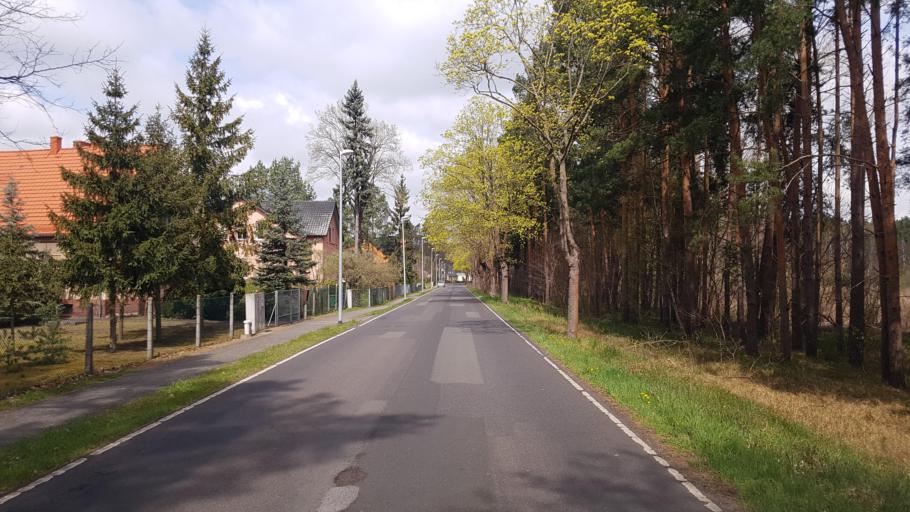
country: DE
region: Brandenburg
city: Luckenwalde
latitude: 52.1209
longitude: 13.1901
